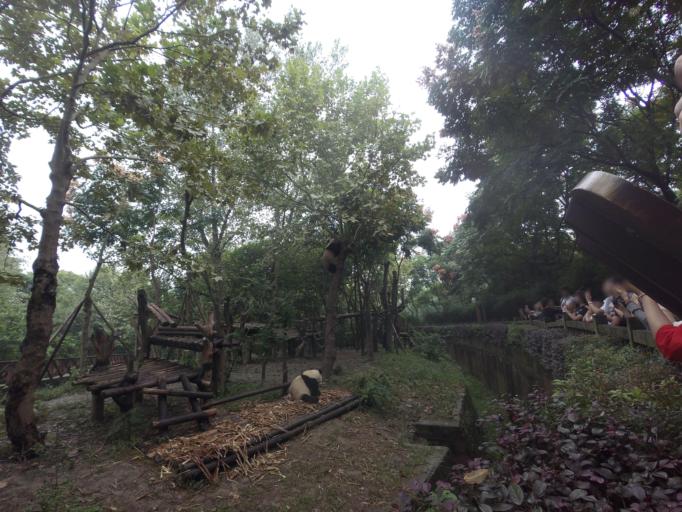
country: CN
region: Sichuan
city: Xindu
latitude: 30.7409
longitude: 104.1388
